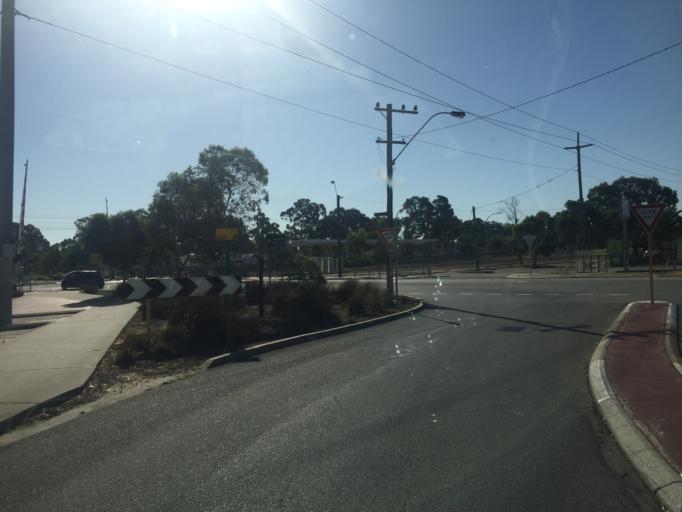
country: AU
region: Western Australia
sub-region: Gosnells
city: Kenwick
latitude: -32.0358
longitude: 115.9699
